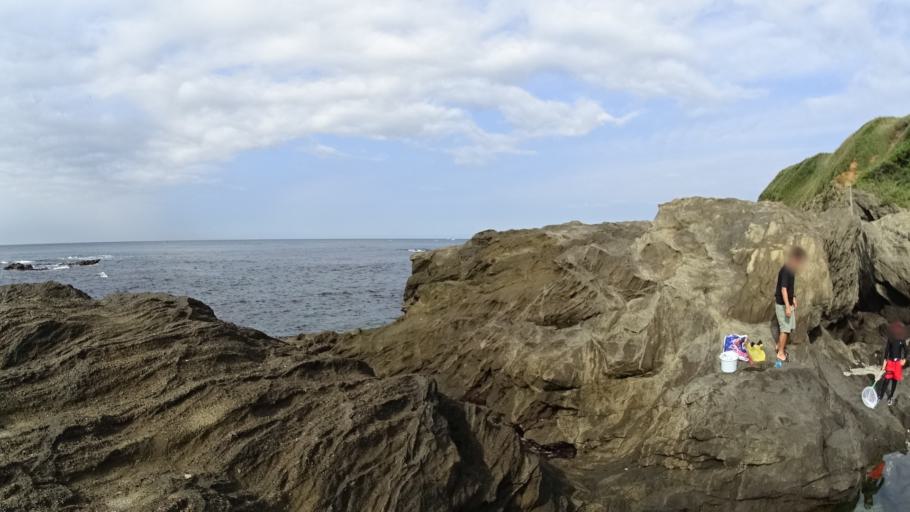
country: JP
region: Kanagawa
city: Miura
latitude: 35.1300
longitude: 139.6259
